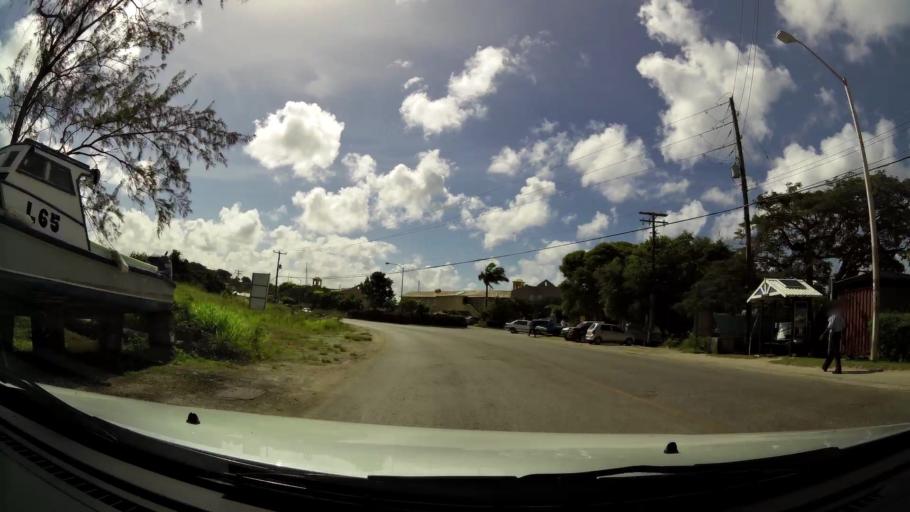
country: BB
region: Saint Peter
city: Speightstown
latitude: 13.2647
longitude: -59.6429
